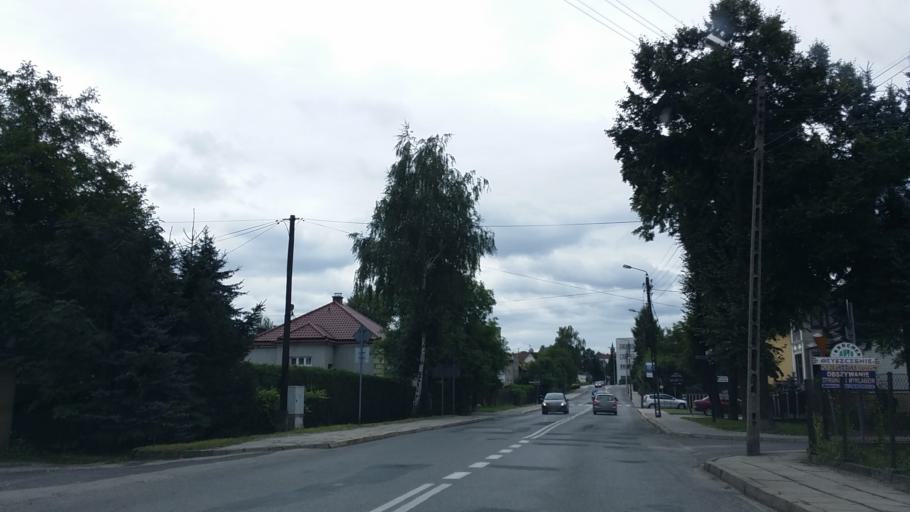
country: PL
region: Lesser Poland Voivodeship
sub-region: Powiat wadowicki
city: Wadowice
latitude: 49.8857
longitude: 19.4844
